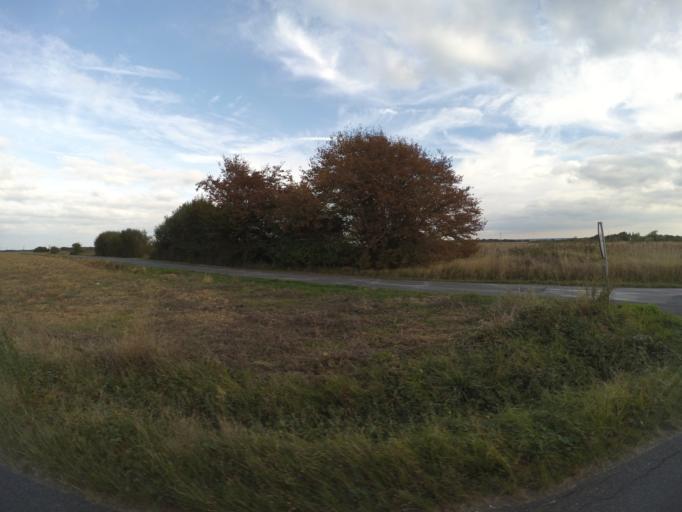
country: FR
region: Centre
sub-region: Departement d'Indre-et-Loire
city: Nazelles-Negron
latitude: 47.4454
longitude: 0.9558
